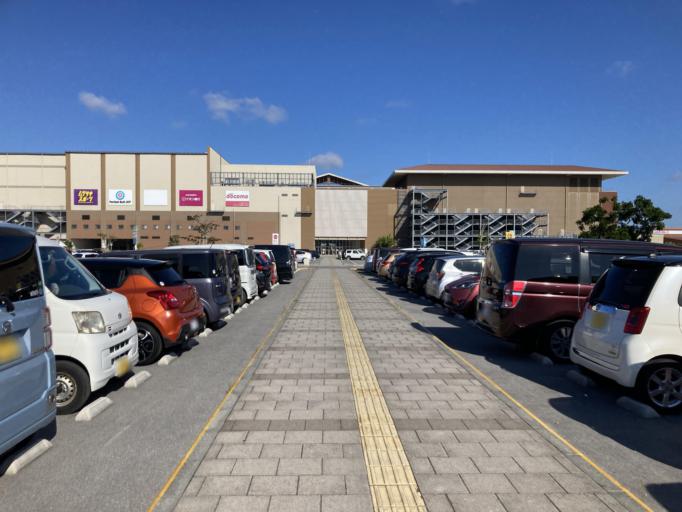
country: JP
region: Okinawa
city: Okinawa
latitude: 26.3124
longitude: 127.7966
